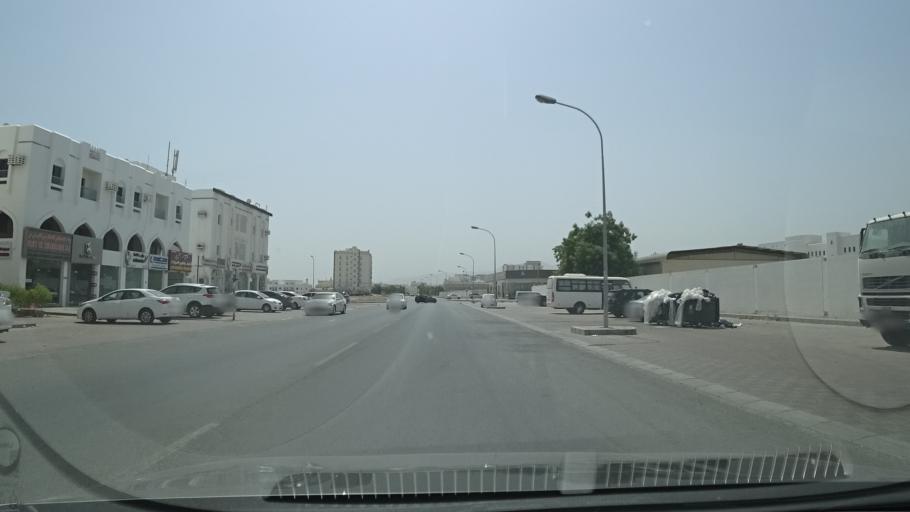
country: OM
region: Muhafazat Masqat
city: Bawshar
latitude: 23.5927
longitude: 58.3707
